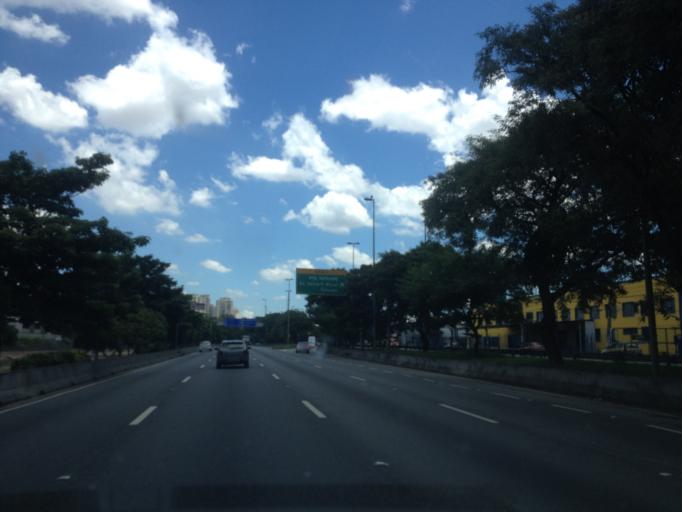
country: BR
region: Sao Paulo
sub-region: Guarulhos
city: Guarulhos
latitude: -23.5241
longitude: -46.5669
